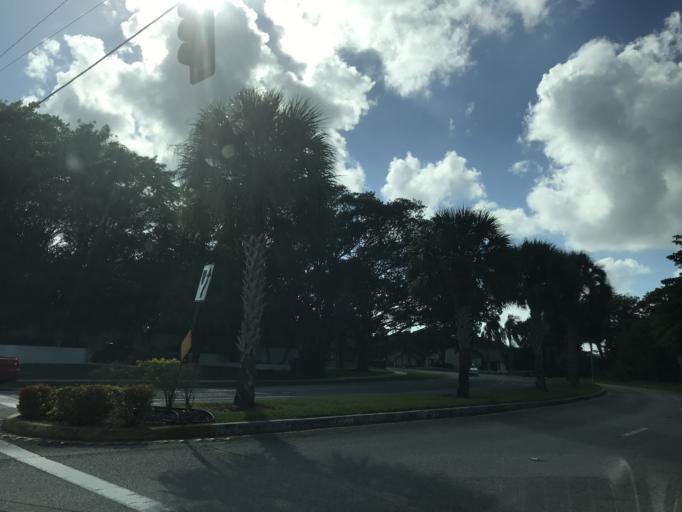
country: US
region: Florida
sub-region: Broward County
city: Coconut Creek
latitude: 26.2511
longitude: -80.1865
